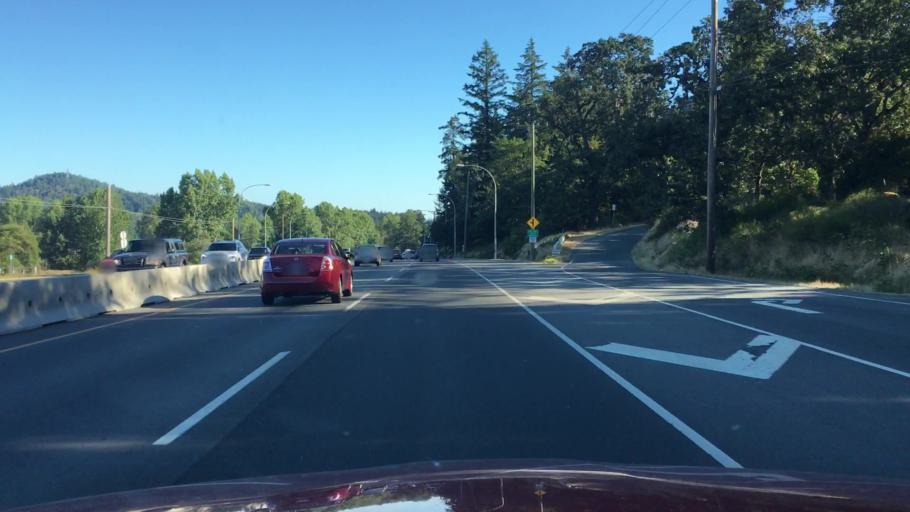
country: CA
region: British Columbia
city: Victoria
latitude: 48.5217
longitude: -123.3858
